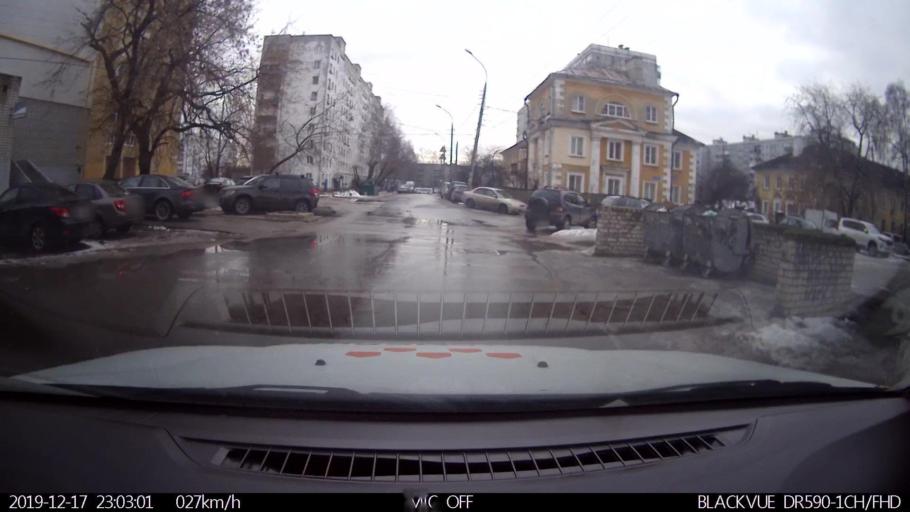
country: RU
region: Nizjnij Novgorod
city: Gorbatovka
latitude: 56.3507
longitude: 43.8511
